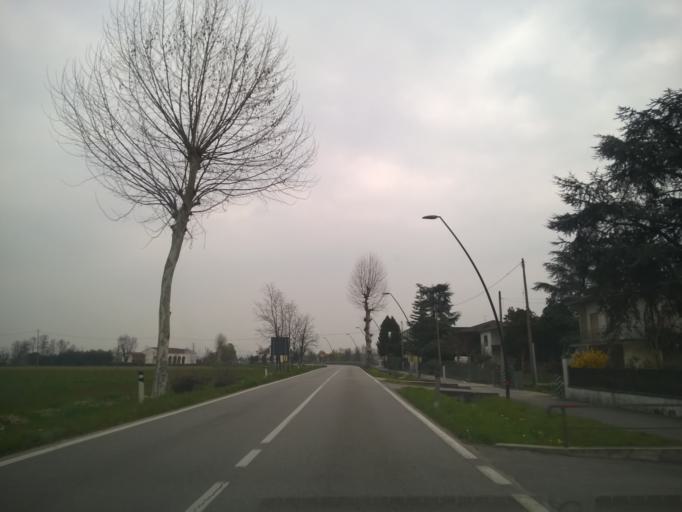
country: IT
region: Veneto
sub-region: Provincia di Padova
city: San Pietro in Gu
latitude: 45.6192
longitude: 11.6779
